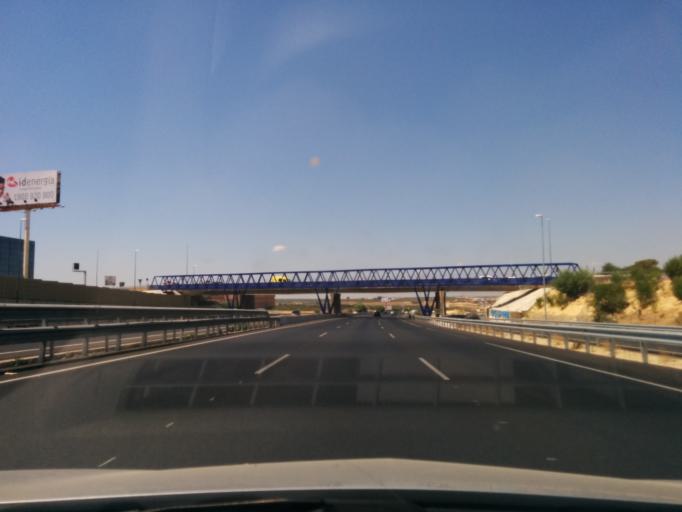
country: ES
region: Andalusia
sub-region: Provincia de Sevilla
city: Bormujos
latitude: 37.3764
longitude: -6.0802
